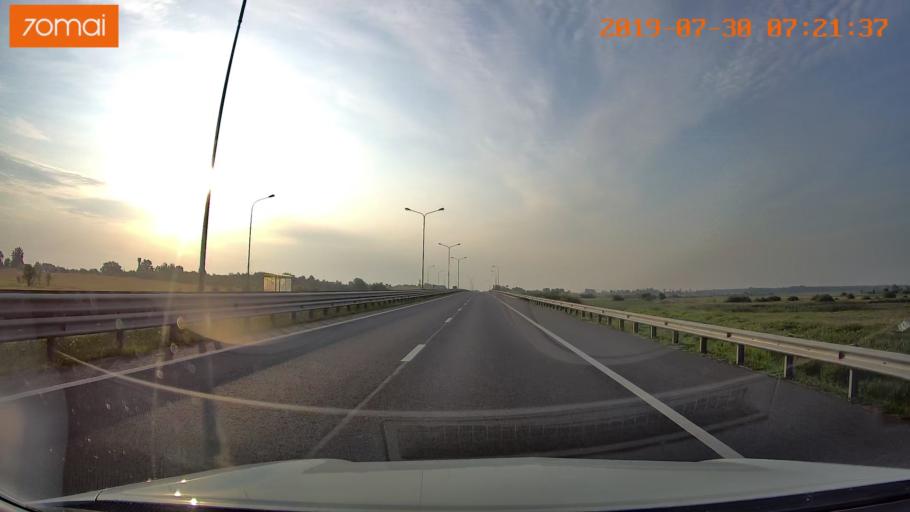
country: RU
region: Kaliningrad
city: Bol'shoe Isakovo
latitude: 54.6956
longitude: 20.7337
